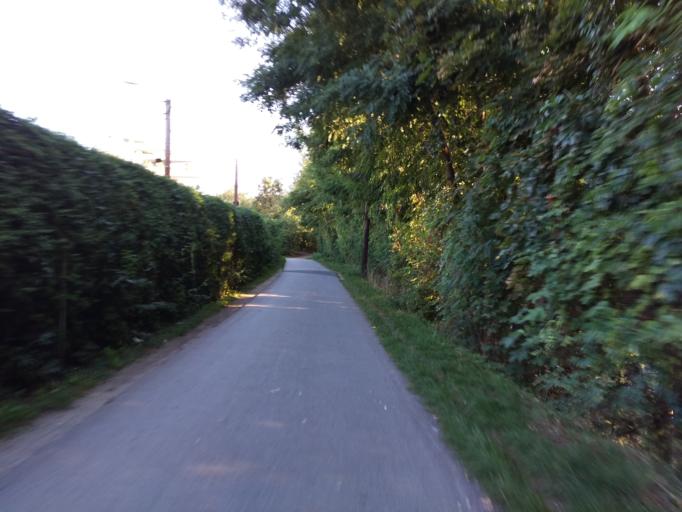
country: AT
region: Styria
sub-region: Graz Stadt
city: Graz
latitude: 47.0545
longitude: 15.4368
